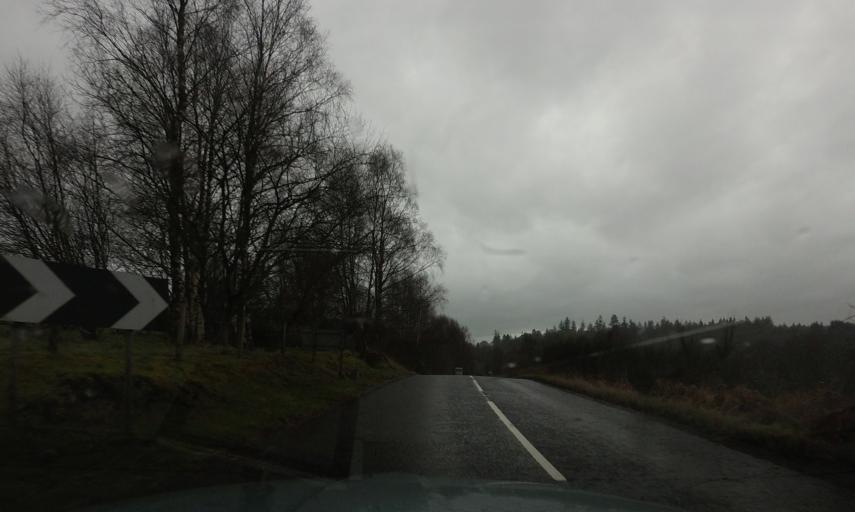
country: GB
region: Scotland
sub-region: Stirling
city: Balfron
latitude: 56.1622
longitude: -4.3622
